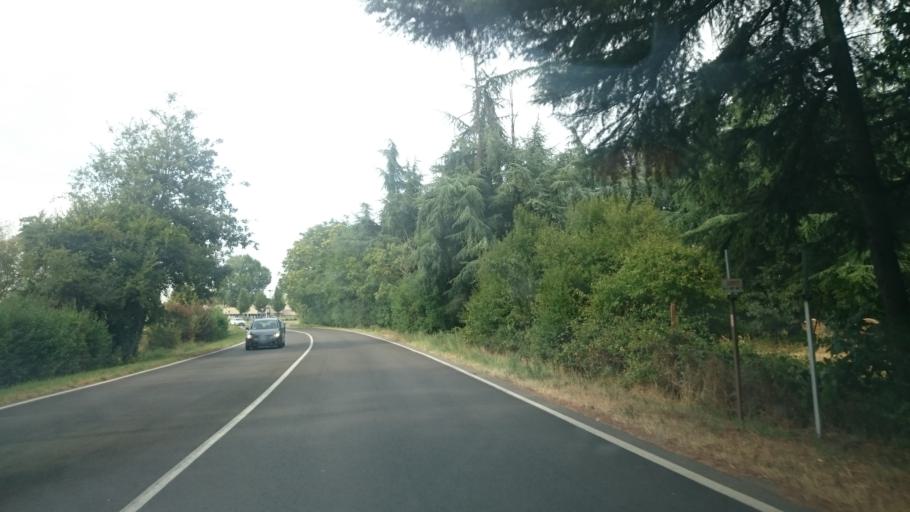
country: IT
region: Emilia-Romagna
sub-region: Provincia di Reggio Emilia
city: Reggio nell'Emilia
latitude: 44.6701
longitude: 10.6012
